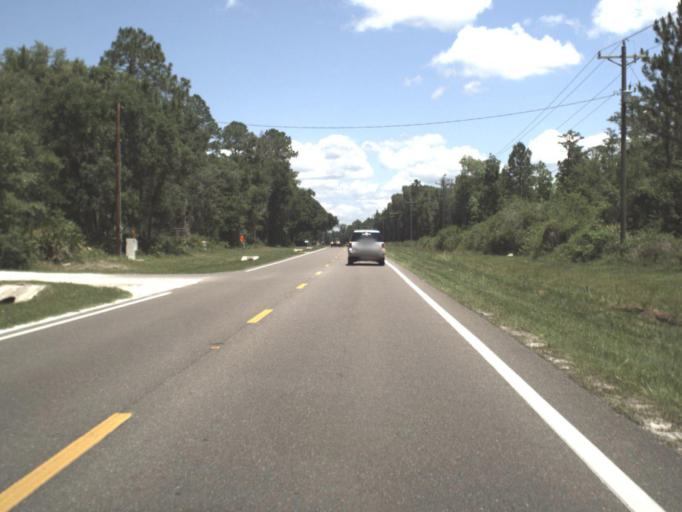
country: US
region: Florida
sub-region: Clay County
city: Keystone Heights
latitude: 29.7423
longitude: -82.0517
